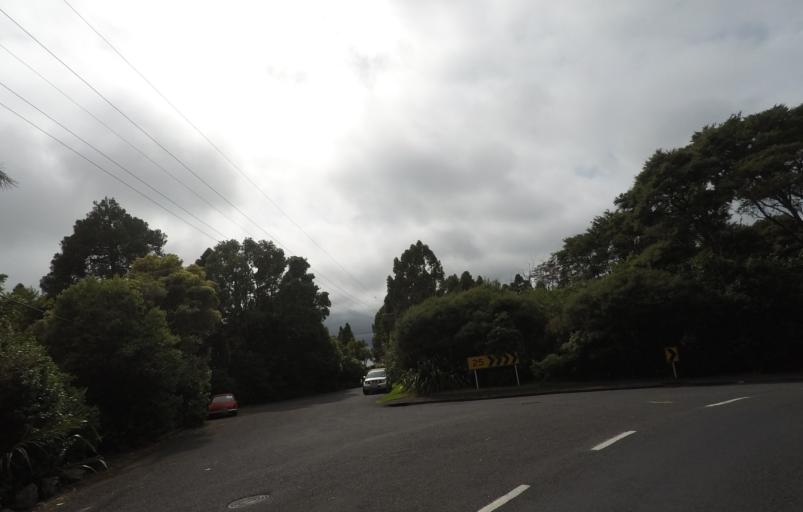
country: NZ
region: Auckland
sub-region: Auckland
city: Titirangi
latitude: -36.9451
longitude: 174.6628
